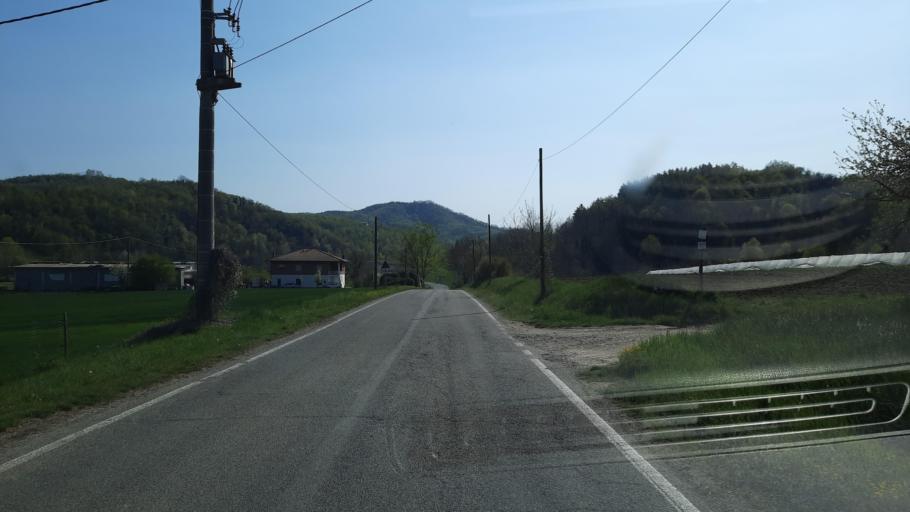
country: IT
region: Piedmont
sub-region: Provincia di Alessandria
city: Moncestino
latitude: 45.1502
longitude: 8.1740
